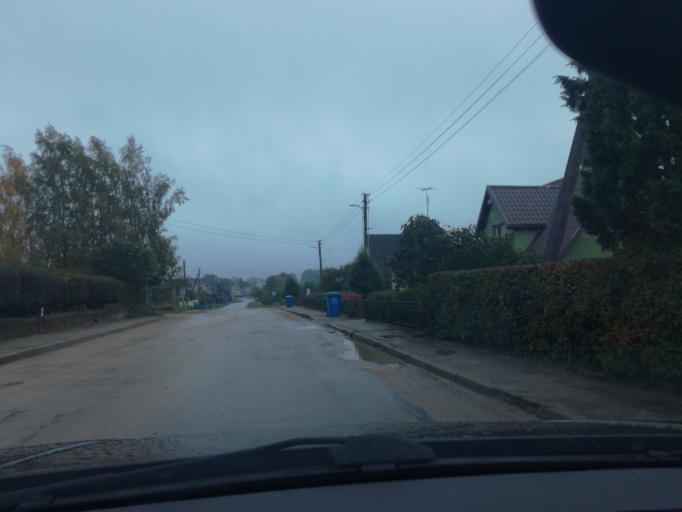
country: LT
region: Alytaus apskritis
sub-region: Alytus
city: Alytus
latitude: 54.3992
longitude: 24.0794
